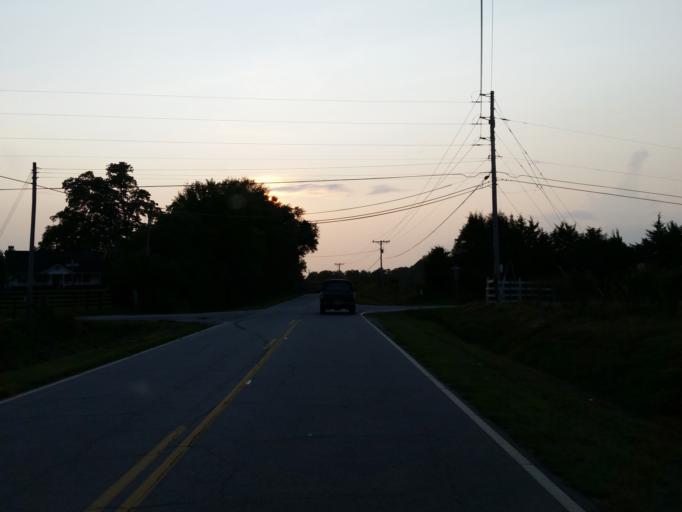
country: US
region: Georgia
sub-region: Henry County
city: Locust Grove
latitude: 33.2815
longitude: -84.1509
